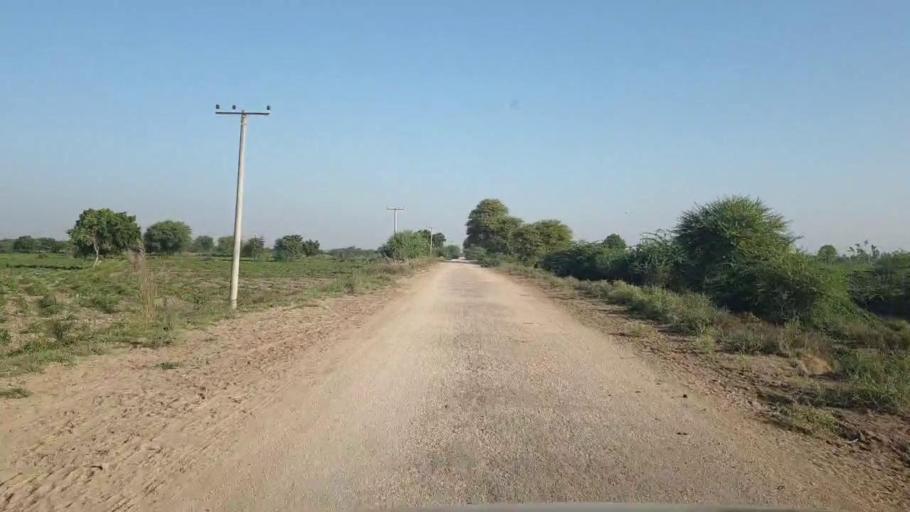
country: PK
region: Sindh
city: Badin
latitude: 24.6915
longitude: 68.8160
